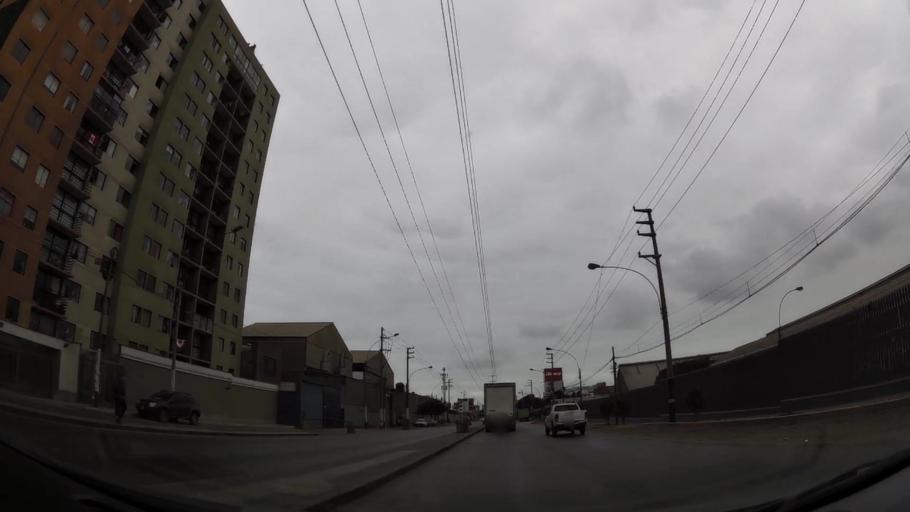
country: PE
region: Callao
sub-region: Callao
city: Callao
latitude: -12.0479
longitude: -77.0930
